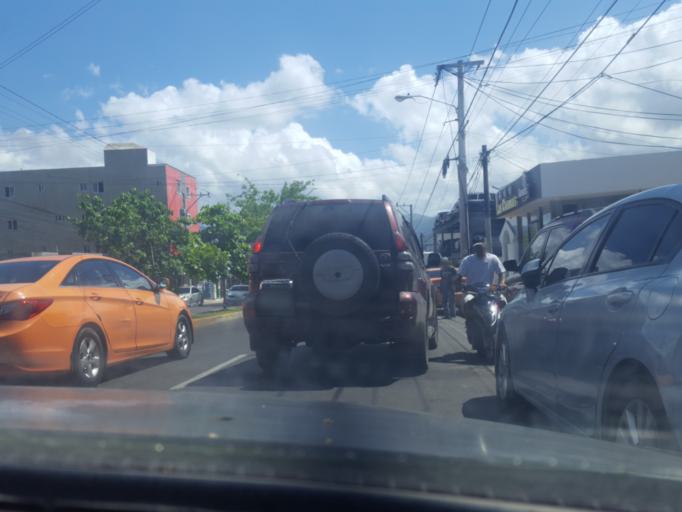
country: DO
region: Santiago
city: Santiago de los Caballeros
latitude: 19.4842
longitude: -70.7045
